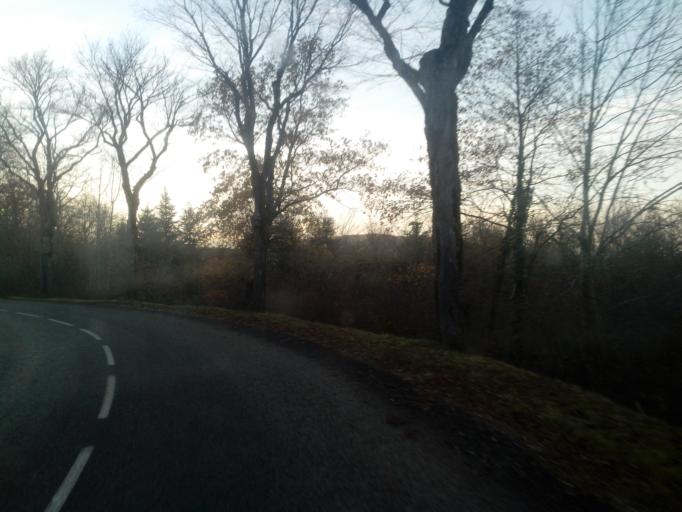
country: FR
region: Languedoc-Roussillon
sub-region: Departement de l'Aude
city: Chalabre
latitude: 42.9097
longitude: 2.0175
